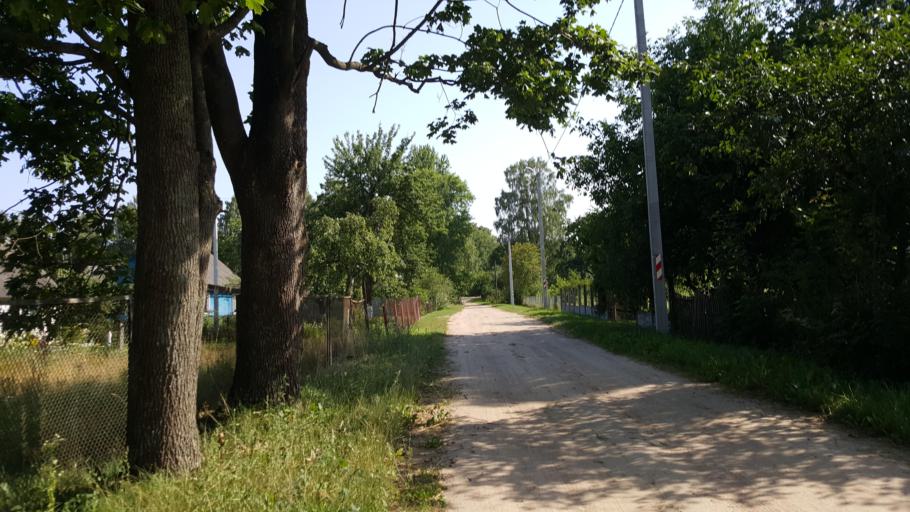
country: BY
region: Brest
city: Zhabinka
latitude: 52.2368
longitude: 24.0071
